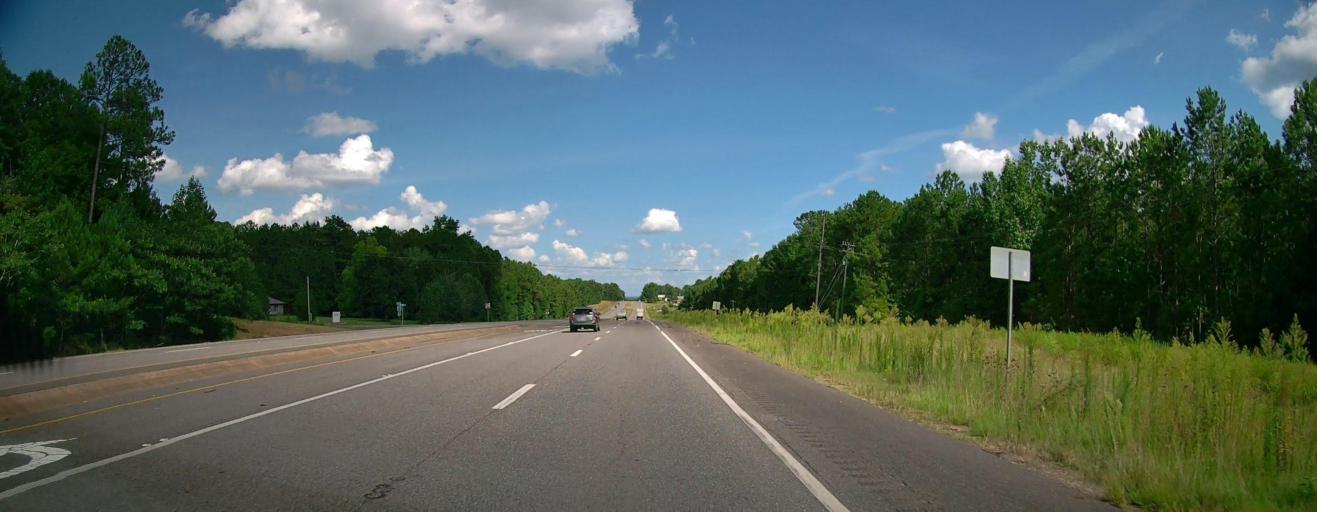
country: US
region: Alabama
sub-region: Tuscaloosa County
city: Northport
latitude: 33.2567
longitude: -87.6960
